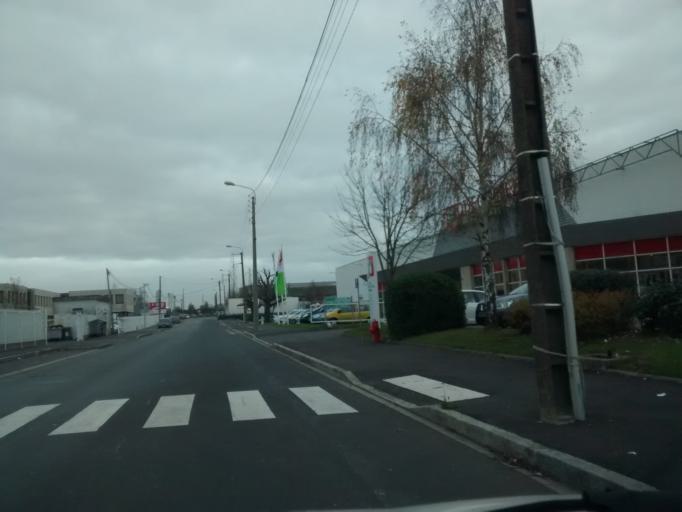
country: FR
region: Brittany
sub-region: Departement d'Ille-et-Vilaine
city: Vezin-le-Coquet
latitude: 48.1080
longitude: -1.7307
